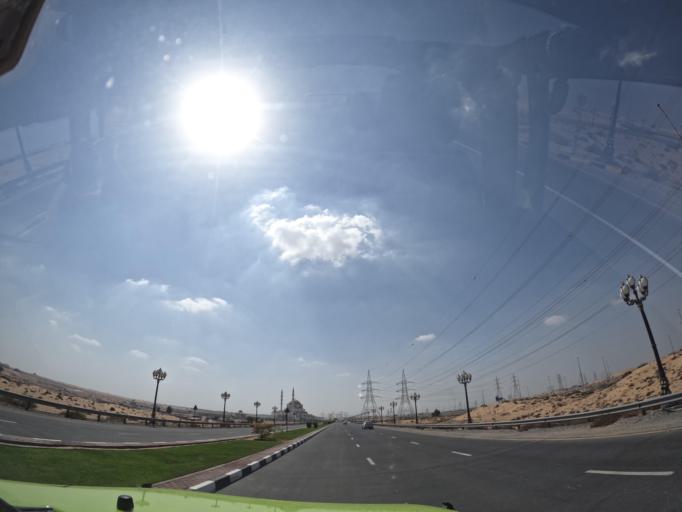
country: AE
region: Ash Shariqah
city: Sharjah
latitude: 25.2473
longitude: 55.5723
